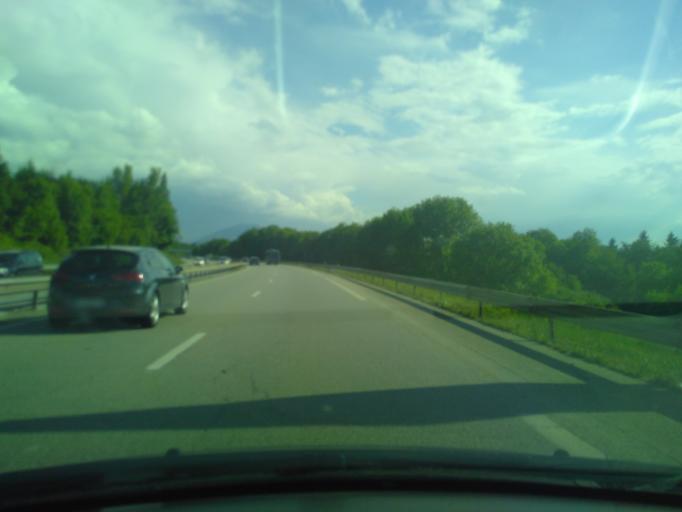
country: FR
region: Rhone-Alpes
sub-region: Departement de la Haute-Savoie
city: Pringy
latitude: 45.9666
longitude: 6.1306
